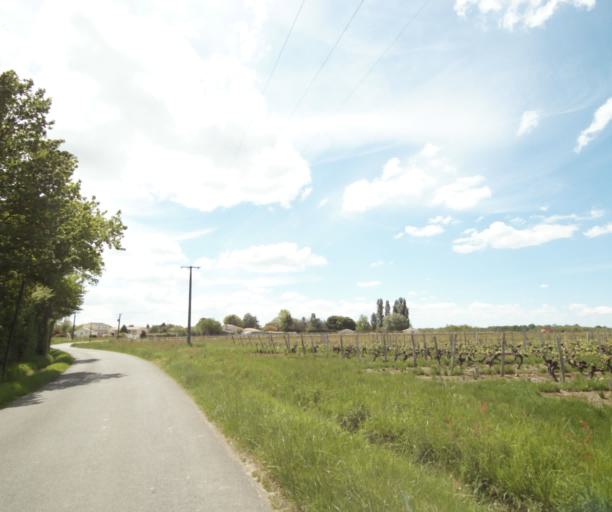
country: FR
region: Poitou-Charentes
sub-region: Departement de la Charente-Maritime
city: Burie
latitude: 45.7506
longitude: -0.4459
